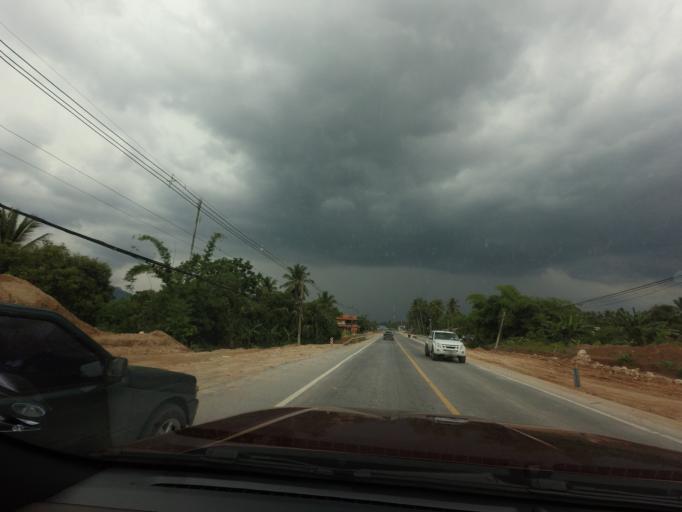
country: TH
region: Yala
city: Krong Pi Nang
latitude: 6.4297
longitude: 101.2783
